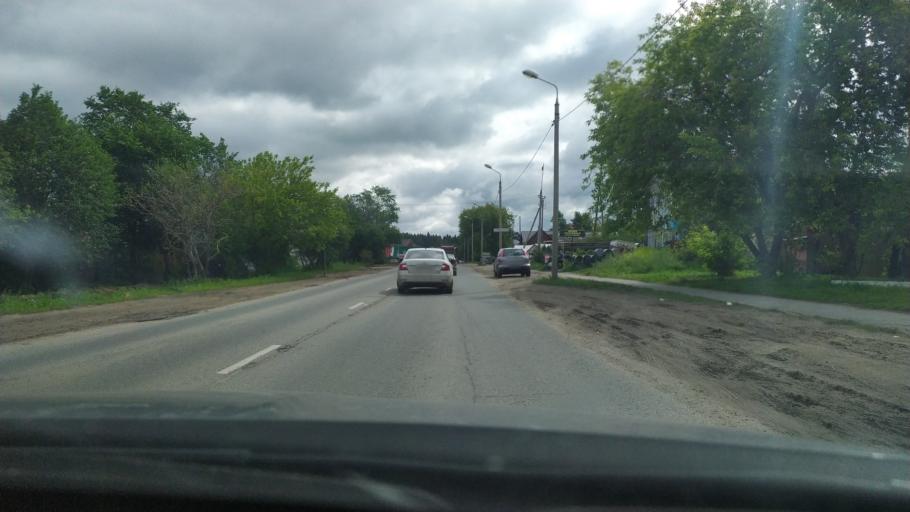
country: RU
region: Perm
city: Froly
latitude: 57.9771
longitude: 56.3085
